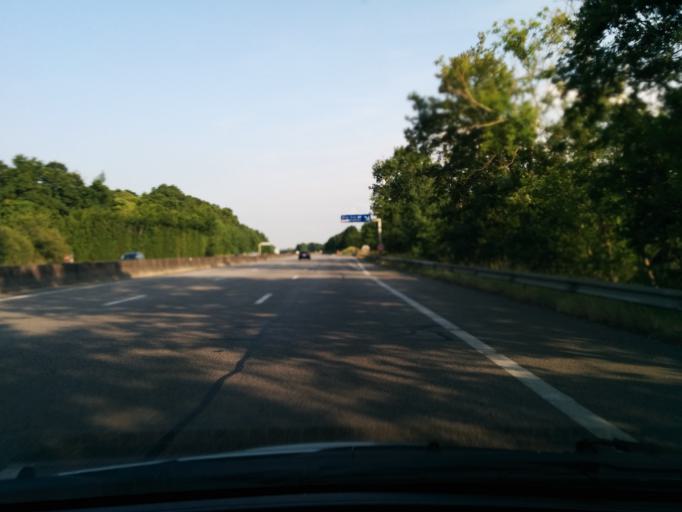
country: FR
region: Haute-Normandie
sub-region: Departement de l'Eure
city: Saint-Aubin-sur-Gaillon
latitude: 49.1079
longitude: 1.3415
